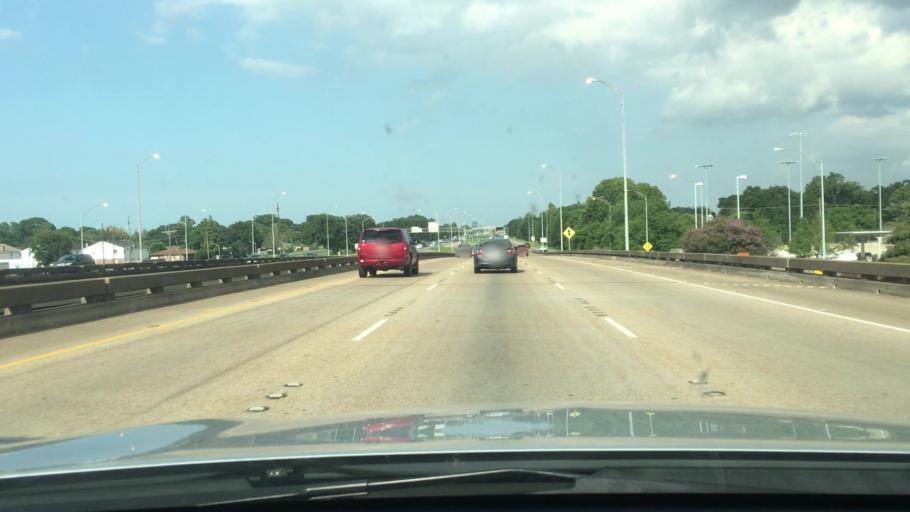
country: US
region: Louisiana
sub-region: Jefferson Parish
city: Kenner
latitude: 30.0076
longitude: -90.2652
